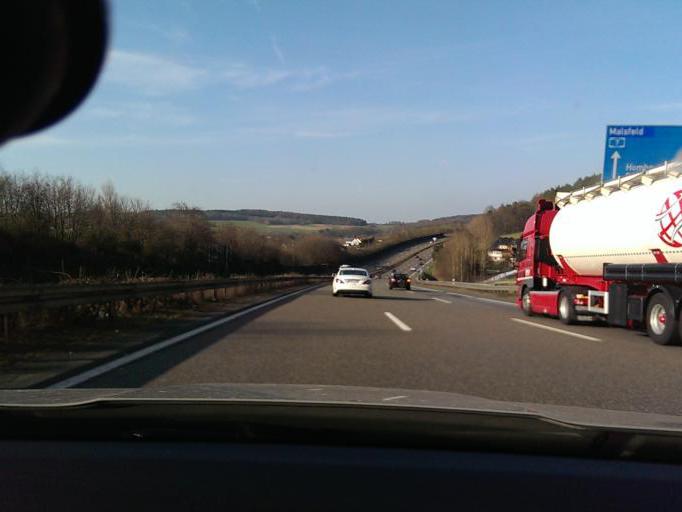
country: DE
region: Hesse
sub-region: Regierungsbezirk Kassel
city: Homberg
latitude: 50.9966
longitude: 9.4743
